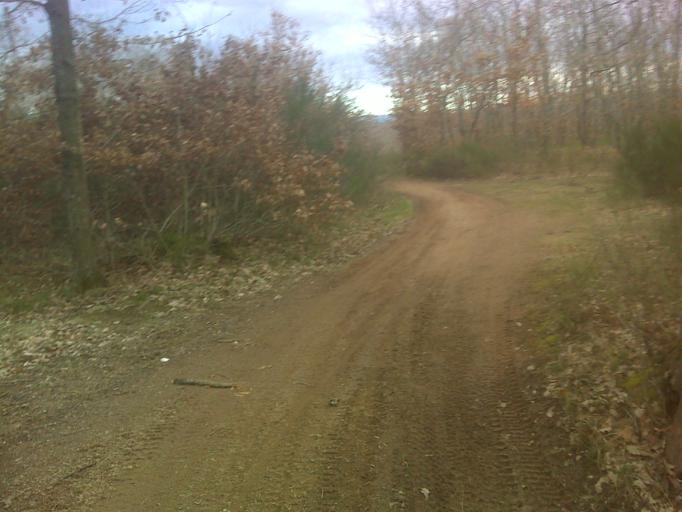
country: FR
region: Rhone-Alpes
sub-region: Departement du Rhone
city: Lentilly
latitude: 45.7930
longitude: 4.6540
